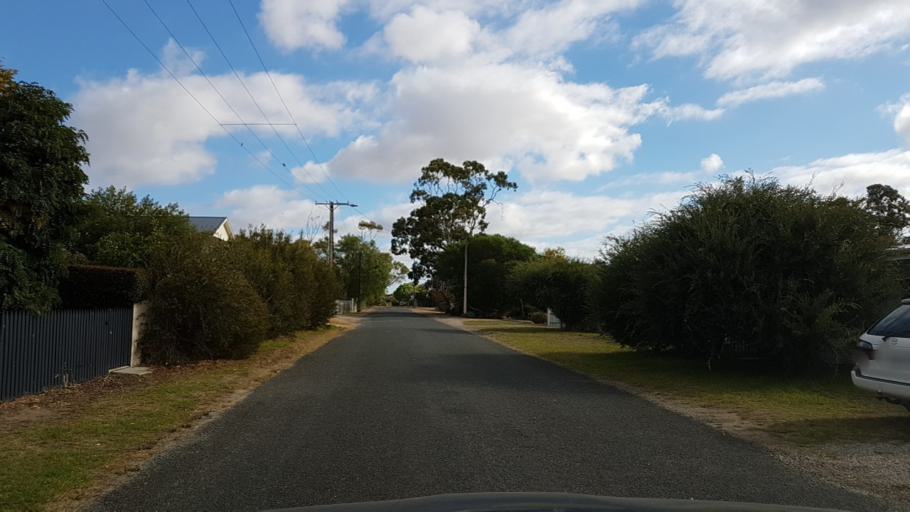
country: AU
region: South Australia
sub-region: Alexandrina
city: Langhorne Creek
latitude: -35.4050
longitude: 138.9760
